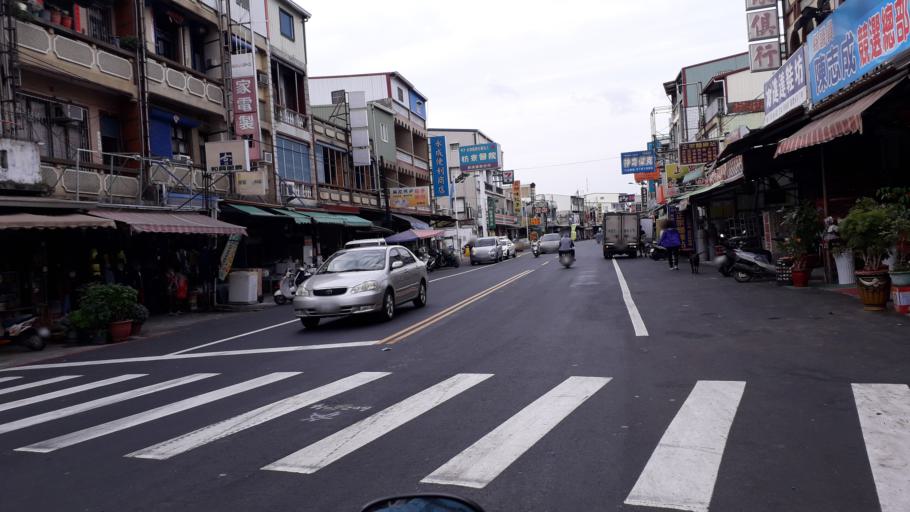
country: TW
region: Taiwan
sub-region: Pingtung
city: Pingtung
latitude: 22.3640
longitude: 120.5973
